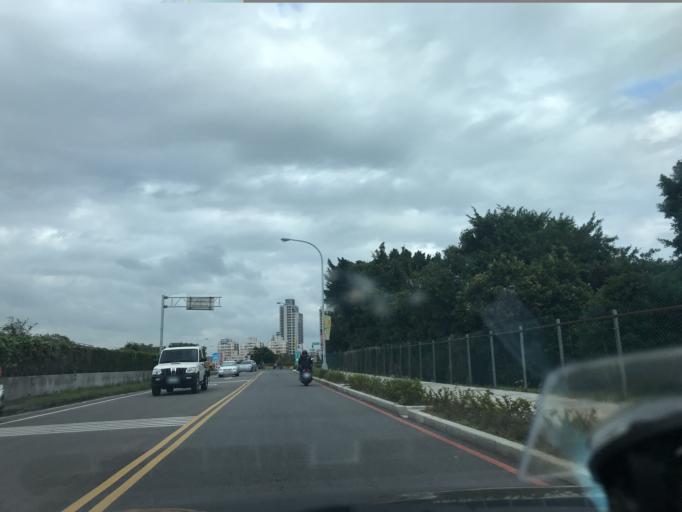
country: TW
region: Taiwan
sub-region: Hsinchu
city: Zhubei
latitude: 24.8275
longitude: 121.0201
